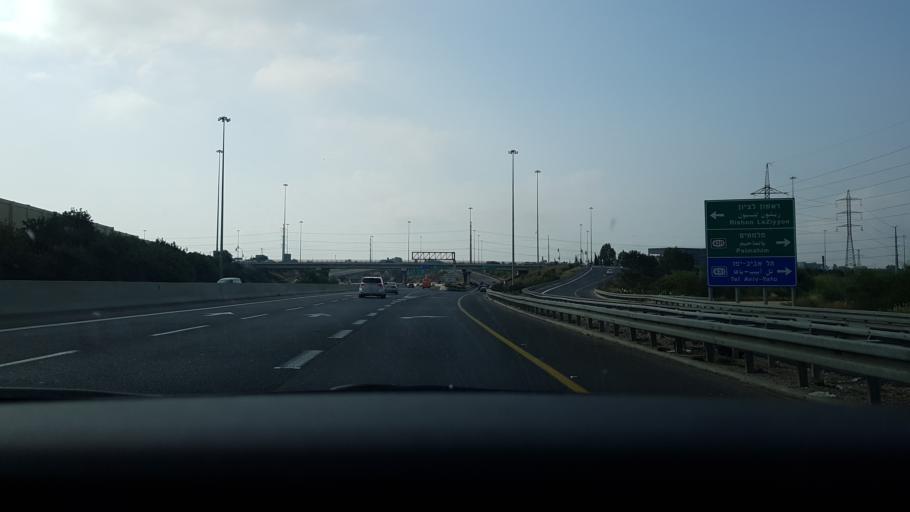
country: IL
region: Central District
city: Rishon LeZiyyon
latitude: 31.9590
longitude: 34.7853
